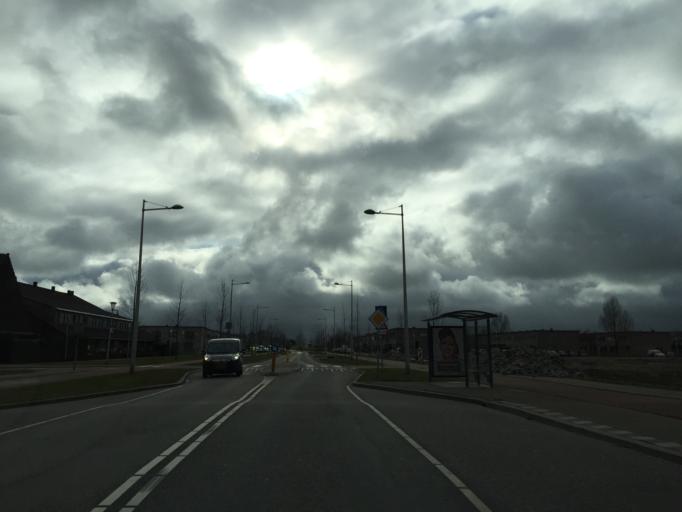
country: NL
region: South Holland
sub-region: Gemeente Lansingerland
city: Berkel en Rodenrijs
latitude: 51.9984
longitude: 4.4614
